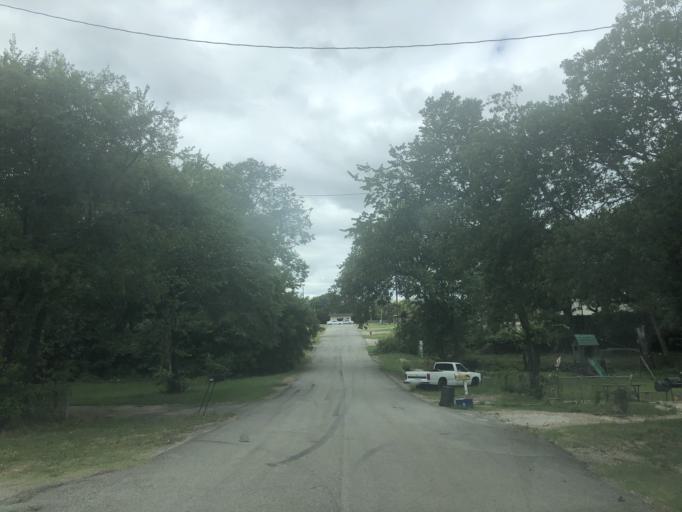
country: US
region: Texas
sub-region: Dallas County
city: Duncanville
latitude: 32.6388
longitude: -96.9067
